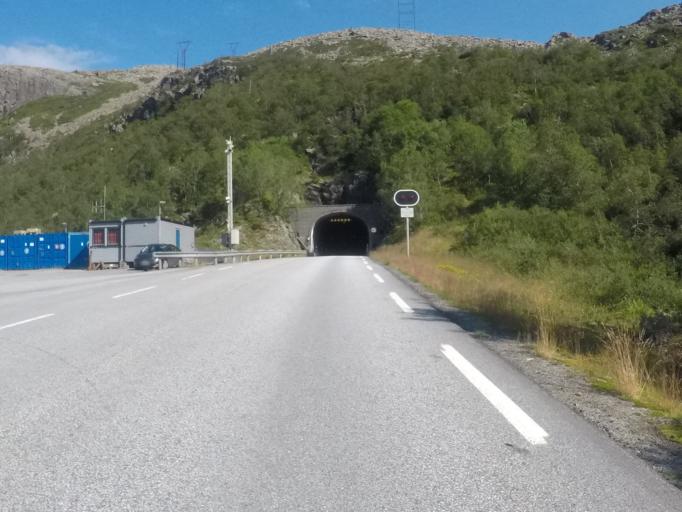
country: NO
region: Sogn og Fjordane
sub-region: Bremanger
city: Svelgen
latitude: 61.6670
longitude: 5.1950
